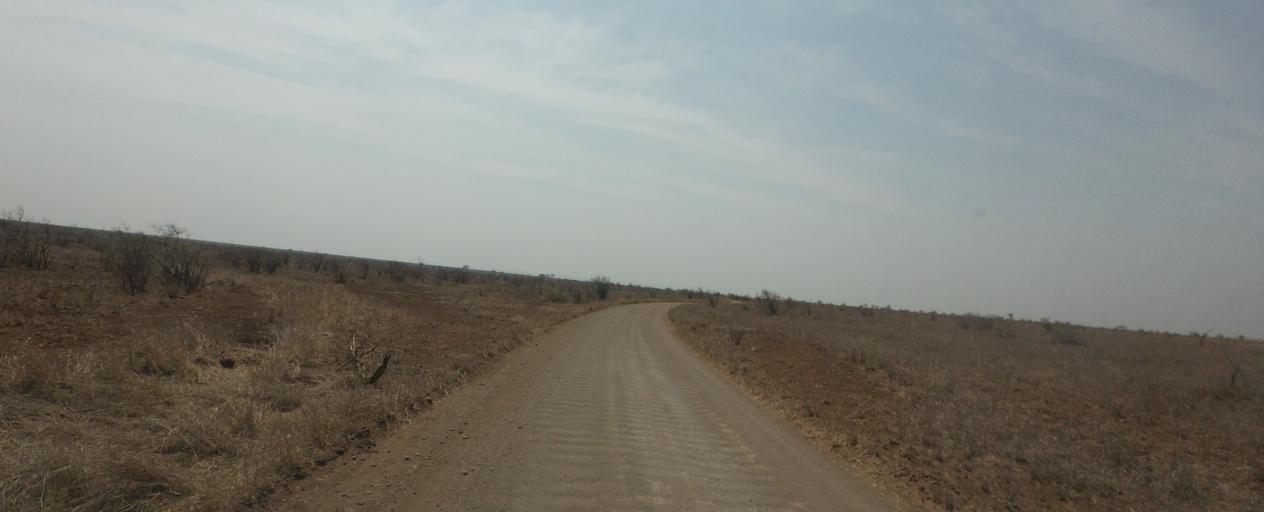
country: ZA
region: Limpopo
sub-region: Mopani District Municipality
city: Phalaborwa
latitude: -24.2534
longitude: 31.7021
